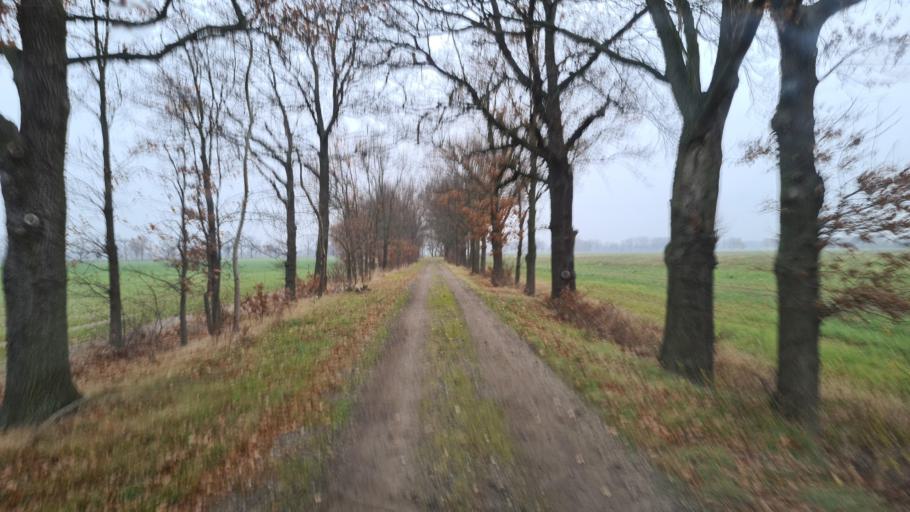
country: DE
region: Brandenburg
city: Schraden
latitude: 51.4122
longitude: 13.7052
